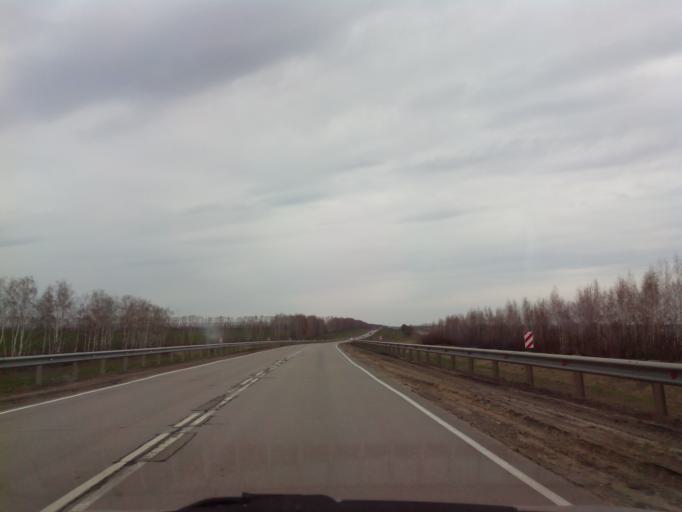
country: RU
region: Tambov
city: Znamenka
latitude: 52.4172
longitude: 41.3773
